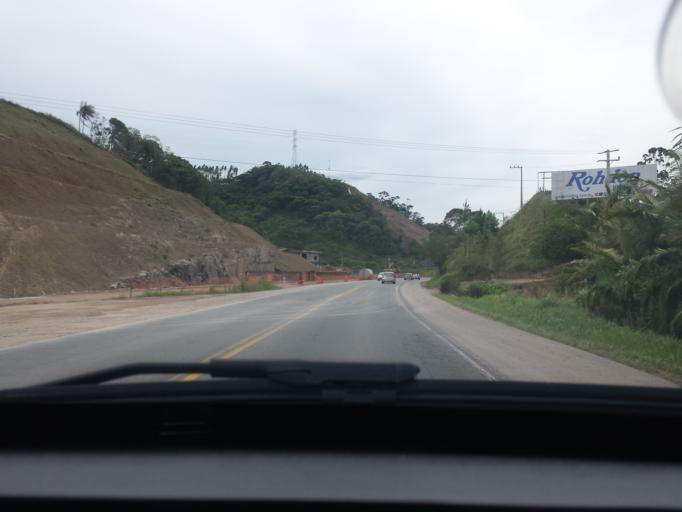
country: BR
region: Santa Catarina
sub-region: Gaspar
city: Gaspar
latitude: -26.8938
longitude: -48.9156
